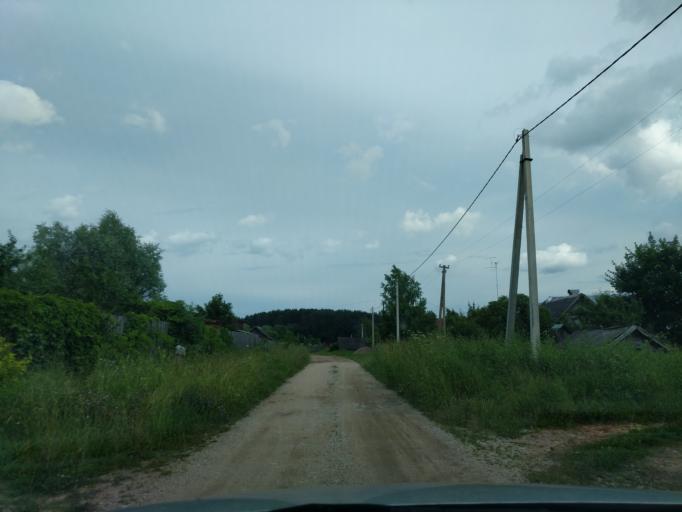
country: RU
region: Kaluga
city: Nikola-Lenivets
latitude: 54.7423
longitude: 35.6386
